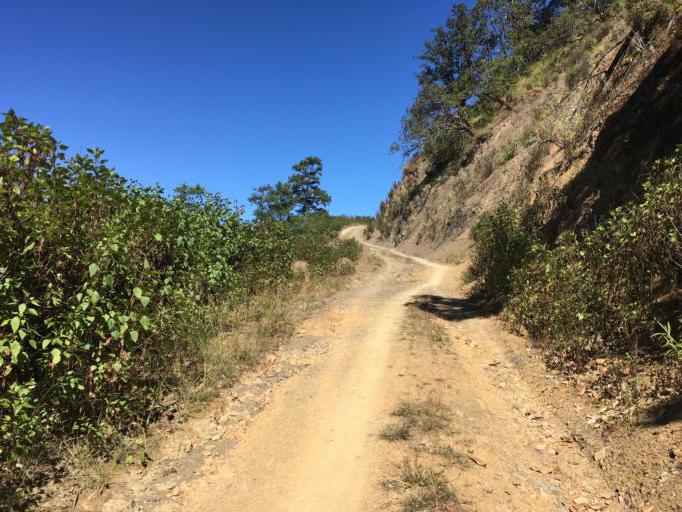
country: MM
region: Chin
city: Hakha
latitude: 22.2694
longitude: 93.6377
